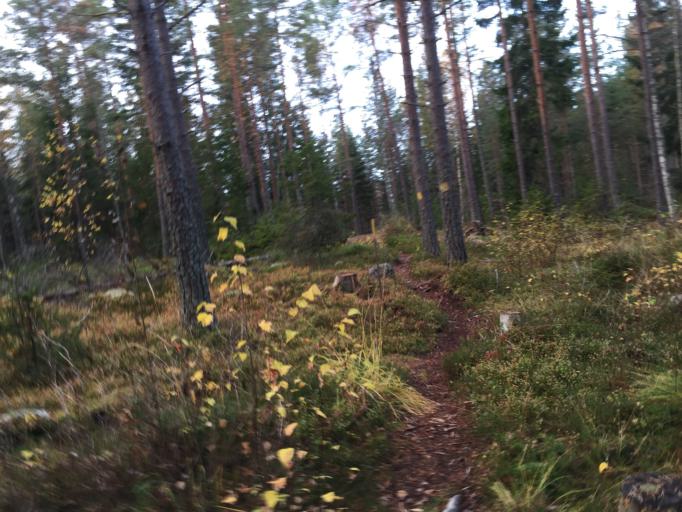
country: SE
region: Vaestmanland
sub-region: Hallstahammars Kommun
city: Hallstahammar
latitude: 59.6346
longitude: 16.2483
